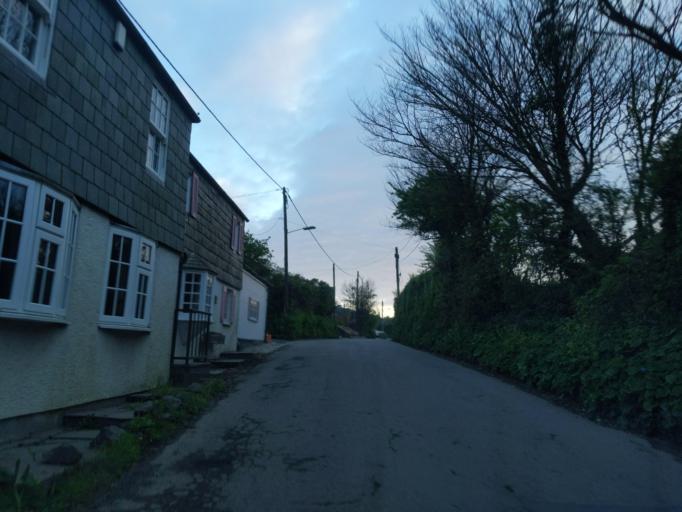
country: GB
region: England
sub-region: Cornwall
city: Polzeath
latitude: 50.5572
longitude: -4.8839
